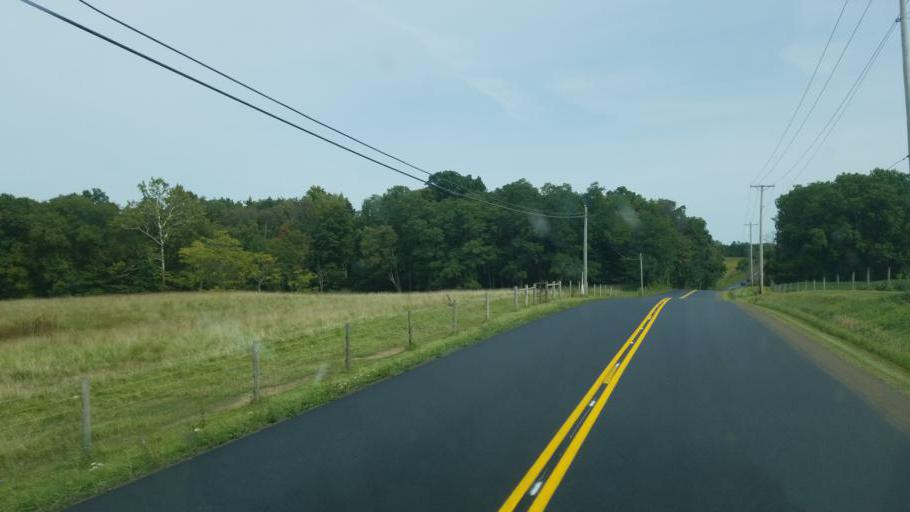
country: US
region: Ohio
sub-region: Knox County
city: Fredericktown
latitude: 40.4038
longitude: -82.6195
